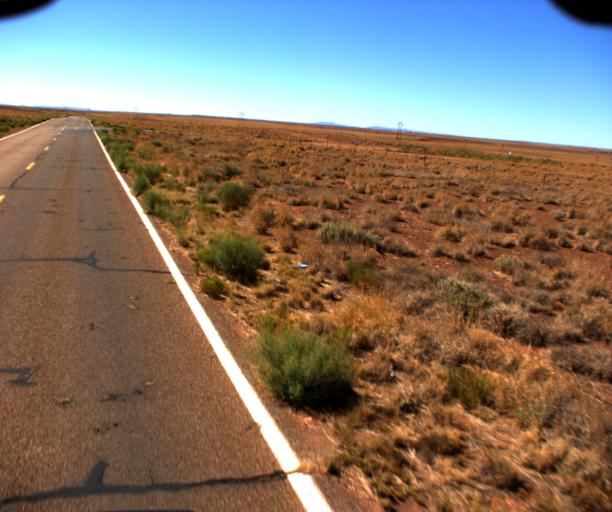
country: US
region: Arizona
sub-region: Coconino County
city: LeChee
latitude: 35.2666
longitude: -110.9722
